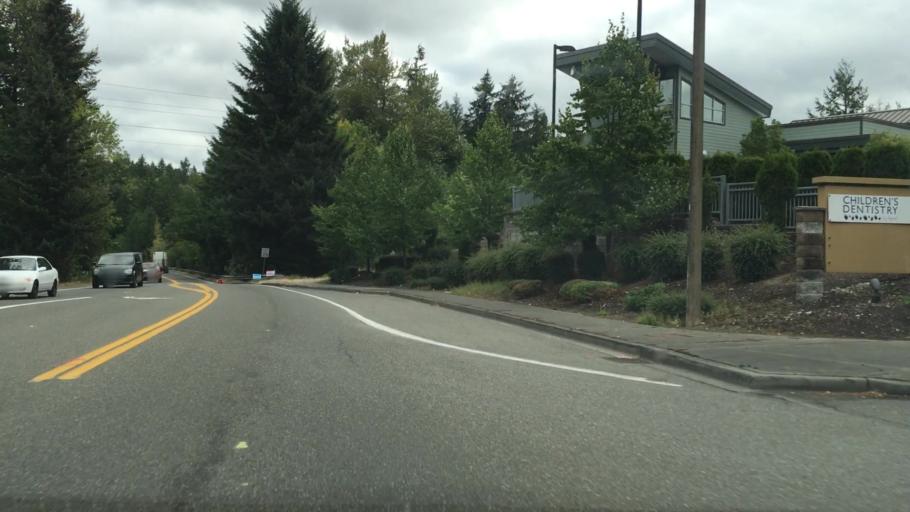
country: US
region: Washington
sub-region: Pierce County
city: DuPont
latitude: 47.0956
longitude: -122.6236
